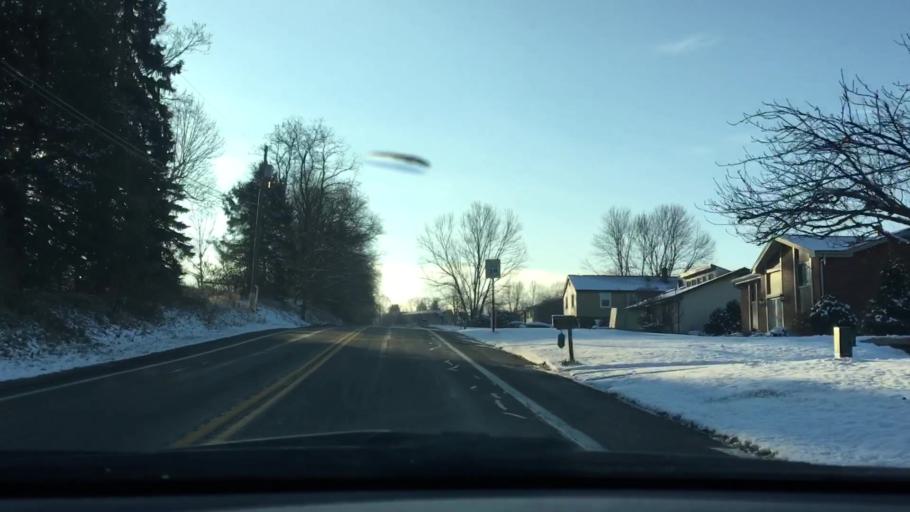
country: US
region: Pennsylvania
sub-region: Allegheny County
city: Elizabeth
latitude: 40.2594
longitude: -79.8482
